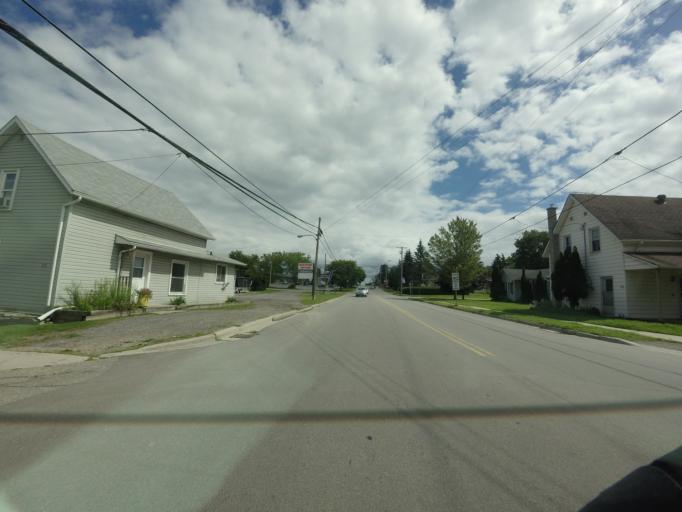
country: CA
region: Ontario
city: Perth
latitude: 44.6741
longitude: -76.3971
